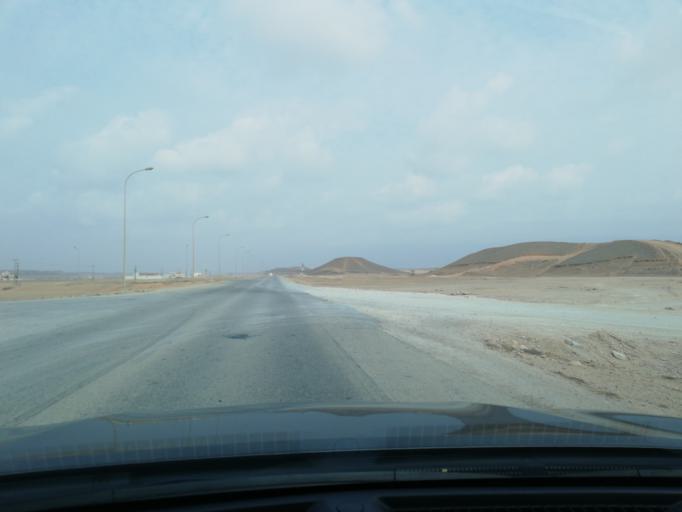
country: OM
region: Zufar
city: Salalah
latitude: 16.9481
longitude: 53.9422
